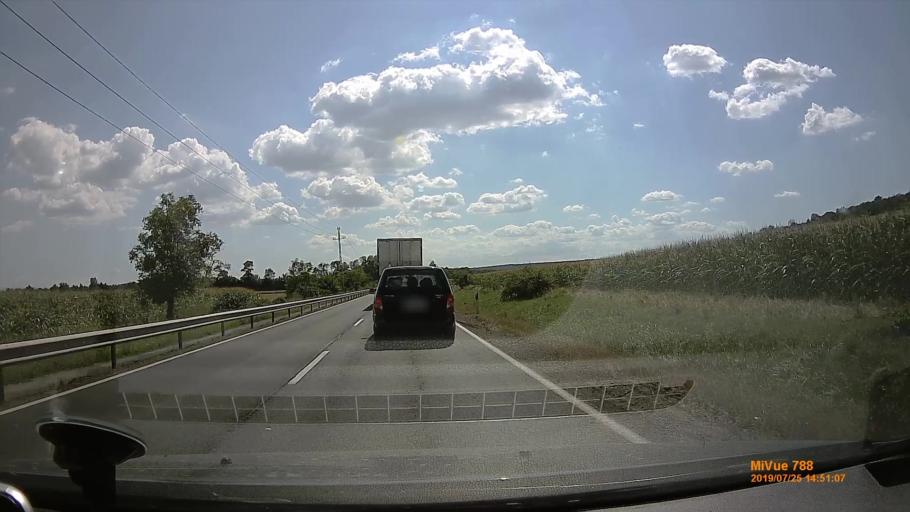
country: HU
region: Borsod-Abauj-Zemplen
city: Aszalo
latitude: 48.2173
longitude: 20.9460
